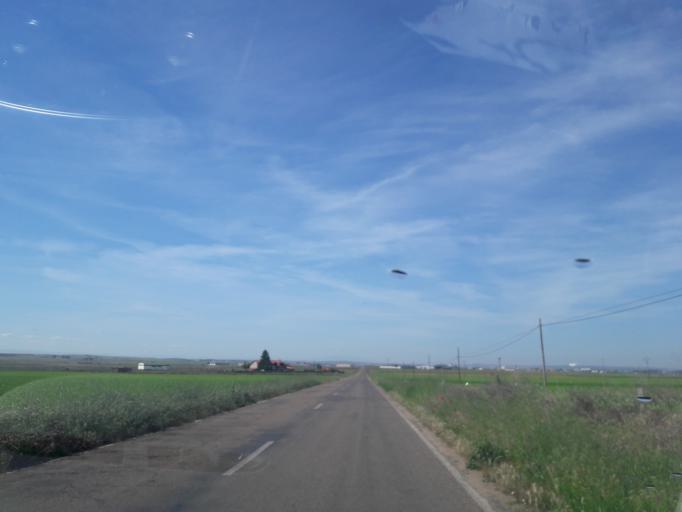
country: ES
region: Castille and Leon
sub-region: Provincia de Salamanca
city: Villoruela
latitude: 41.0039
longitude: -5.3981
